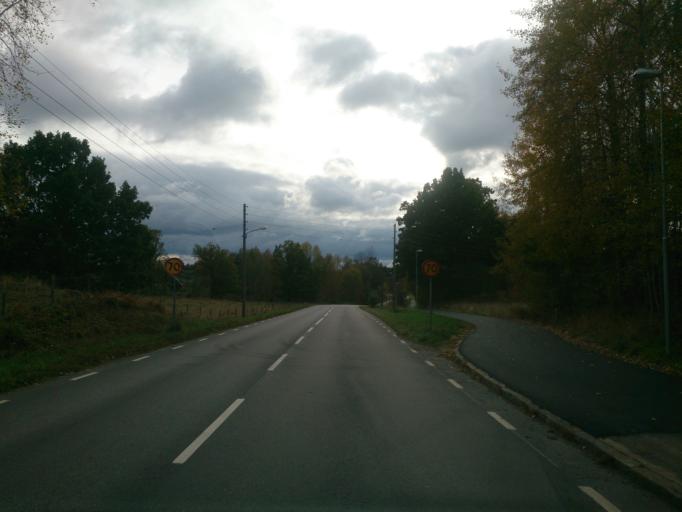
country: SE
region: OEstergoetland
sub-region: Atvidabergs Kommun
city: Atvidaberg
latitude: 58.2162
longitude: 16.0178
